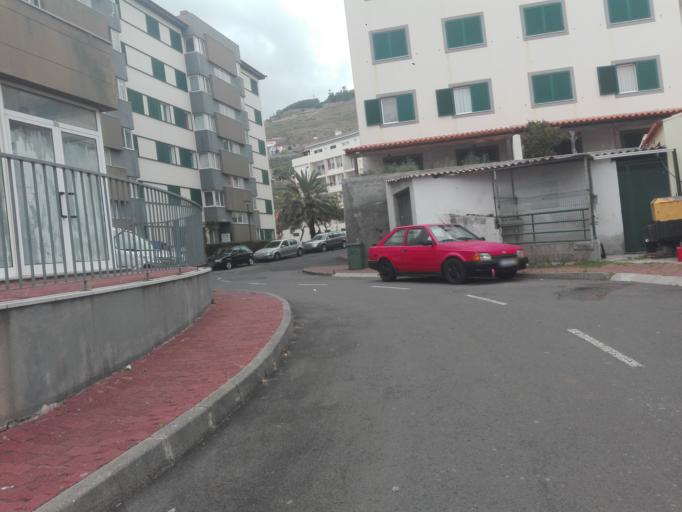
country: PT
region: Madeira
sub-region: Santa Cruz
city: Camacha
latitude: 32.6552
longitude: -16.8270
